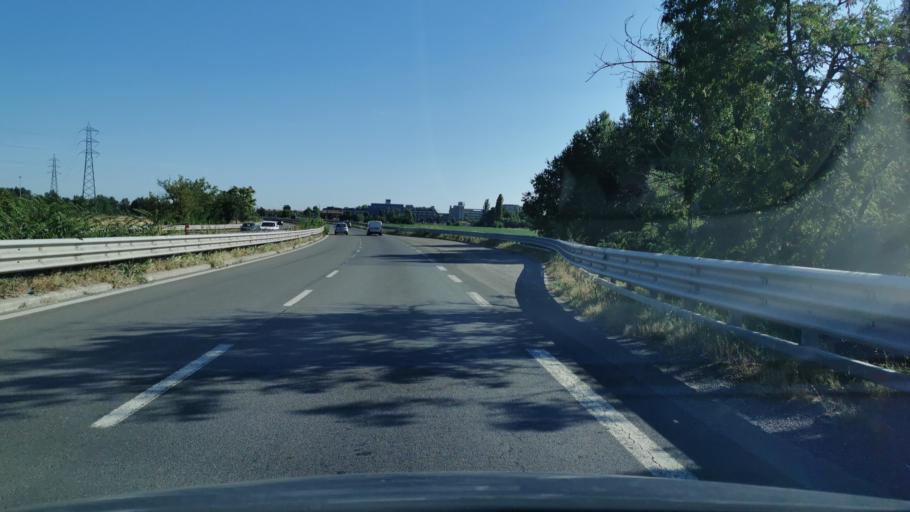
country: IT
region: Emilia-Romagna
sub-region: Provincia di Modena
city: Baggiovara
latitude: 44.6314
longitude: 10.8814
